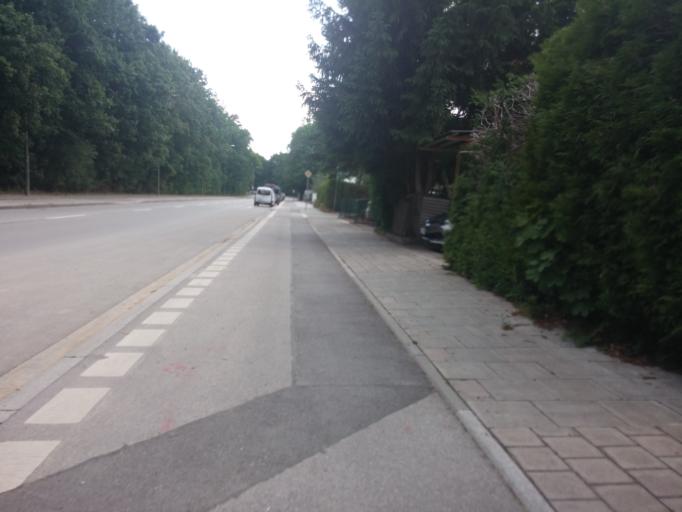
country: DE
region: Bavaria
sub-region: Upper Bavaria
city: Unterhaching
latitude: 48.0866
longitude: 11.5976
